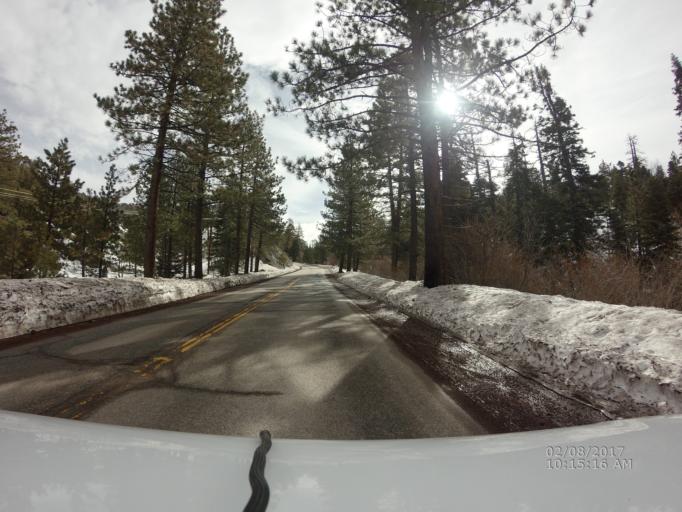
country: US
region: California
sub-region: San Bernardino County
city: Wrightwood
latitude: 34.3832
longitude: -117.7011
